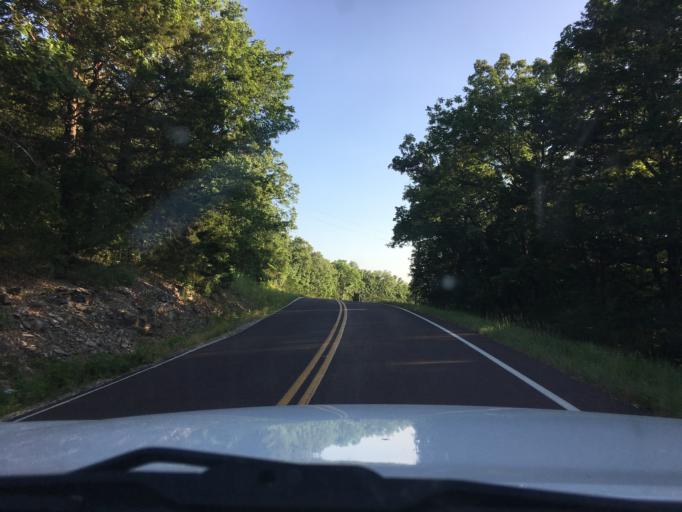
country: US
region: Missouri
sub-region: Gasconade County
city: Owensville
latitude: 38.4529
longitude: -91.6332
